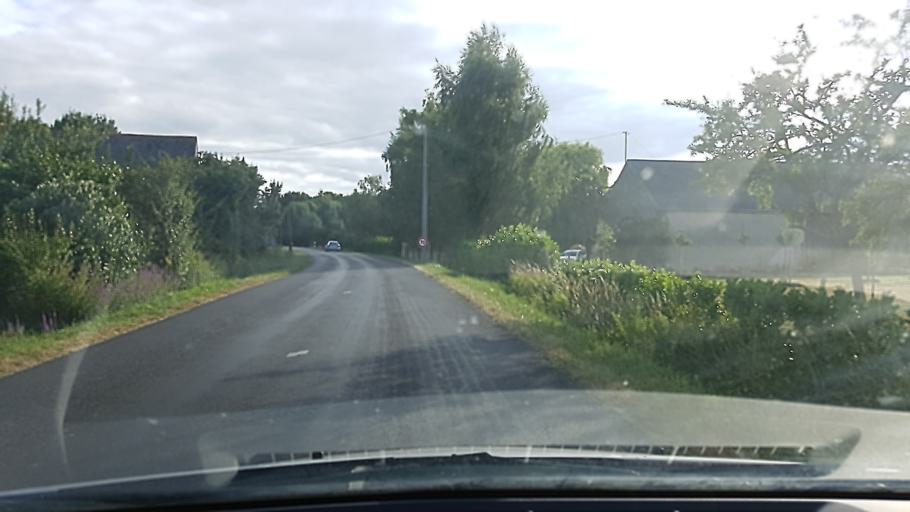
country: FR
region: Pays de la Loire
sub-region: Departement de Maine-et-Loire
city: Maze
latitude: 47.4523
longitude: -0.2796
